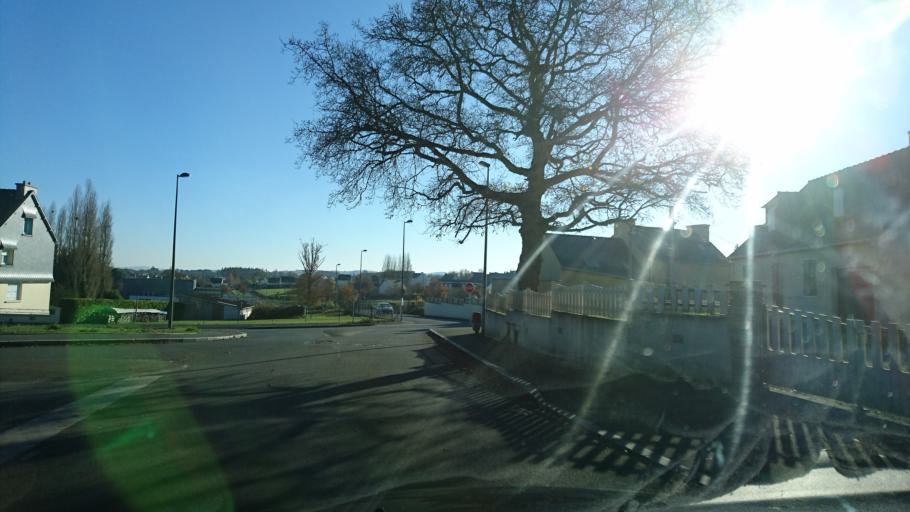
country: FR
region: Brittany
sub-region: Departement des Cotes-d'Armor
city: Pledran
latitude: 48.4498
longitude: -2.7458
